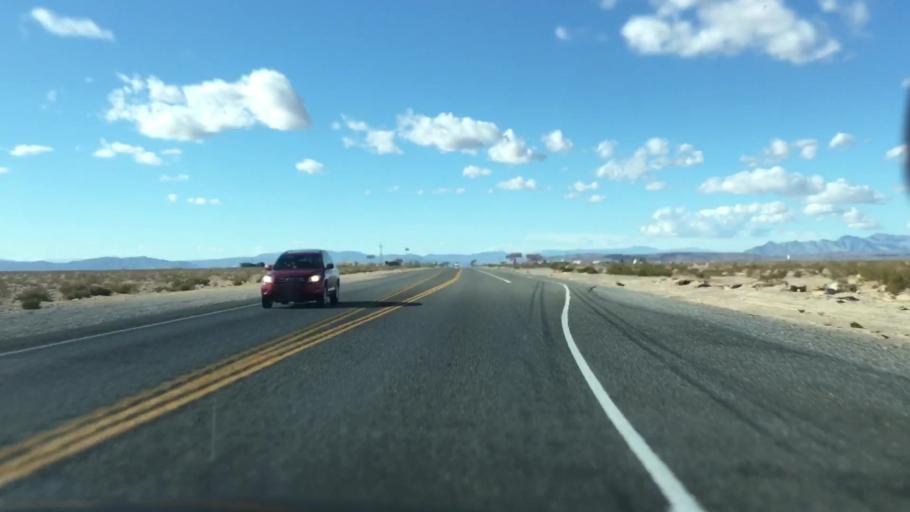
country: US
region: Nevada
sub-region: Nye County
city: Beatty
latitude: 36.6400
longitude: -116.3842
